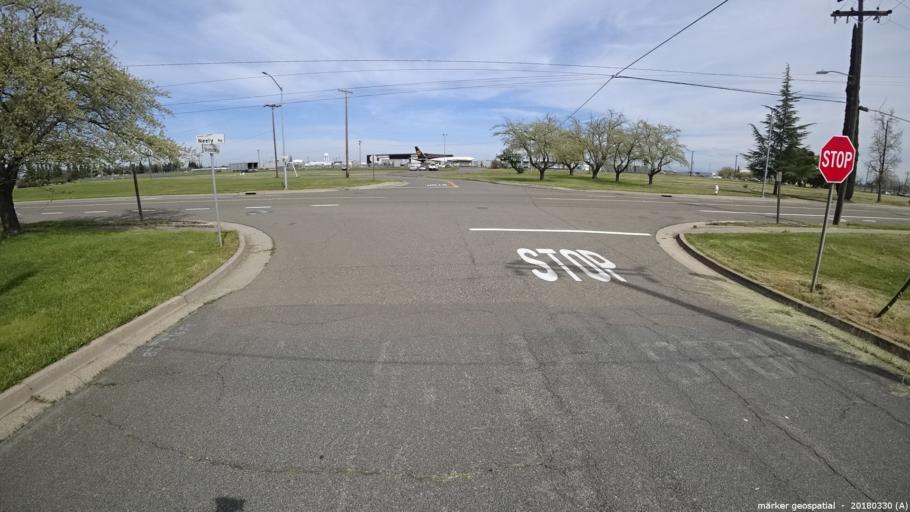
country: US
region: California
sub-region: Sacramento County
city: Rancho Cordova
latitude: 38.5596
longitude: -121.3101
